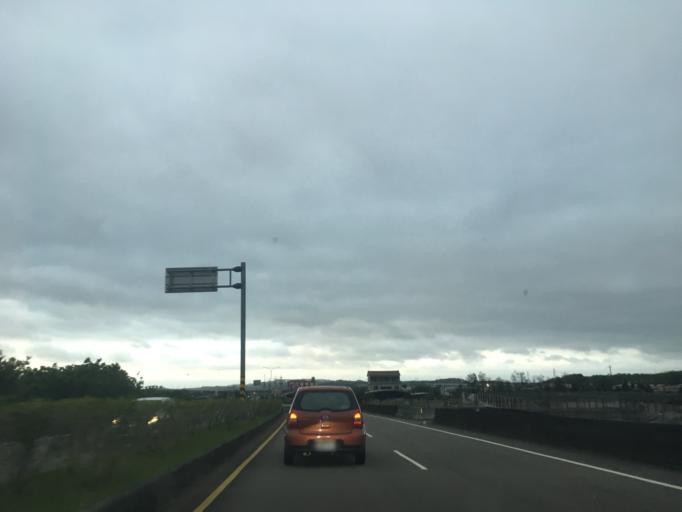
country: TW
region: Taiwan
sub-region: Miaoli
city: Miaoli
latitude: 24.4641
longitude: 120.7813
